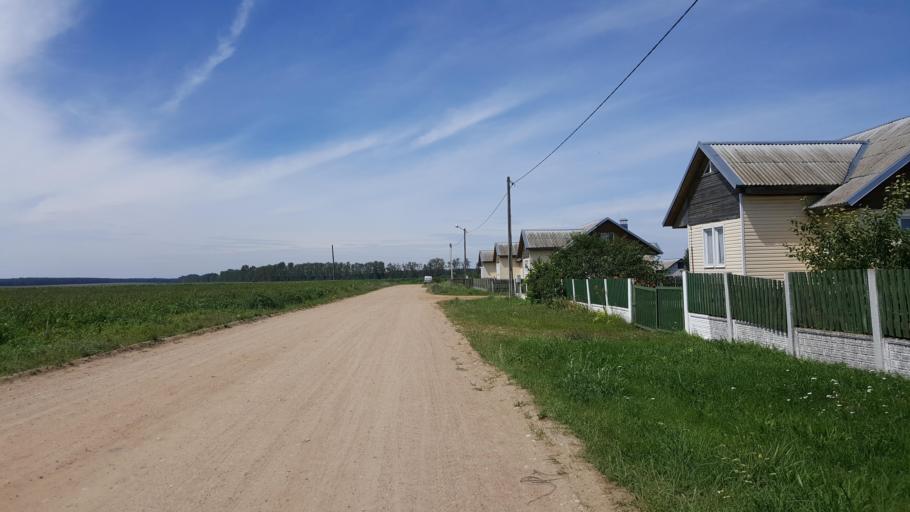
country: BY
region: Brest
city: Pruzhany
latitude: 52.5519
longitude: 24.2021
